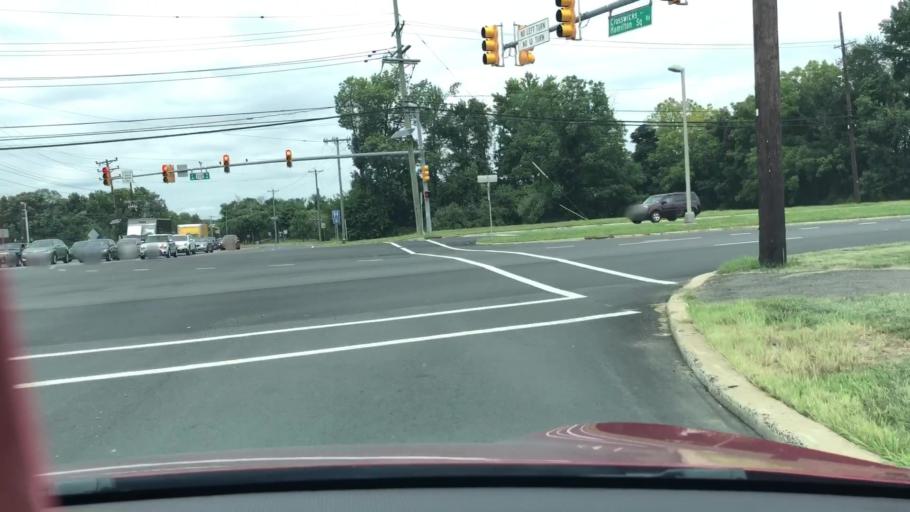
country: US
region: New Jersey
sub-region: Mercer County
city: Yardville
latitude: 40.1929
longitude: -74.6459
